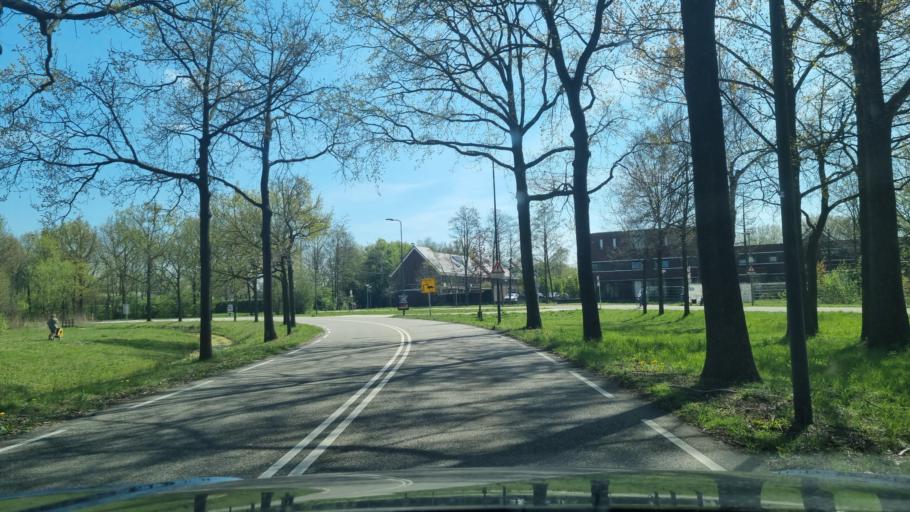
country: NL
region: North Brabant
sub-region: Gemeente 's-Hertogenbosch
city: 's-Hertogenbosch
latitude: 51.7136
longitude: 5.3712
